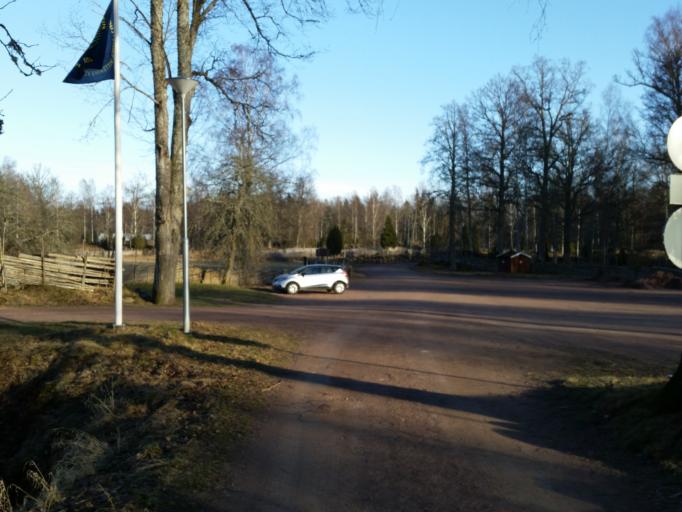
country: SE
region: Kalmar
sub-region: Oskarshamns Kommun
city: Oskarshamn
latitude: 57.3449
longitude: 16.4663
